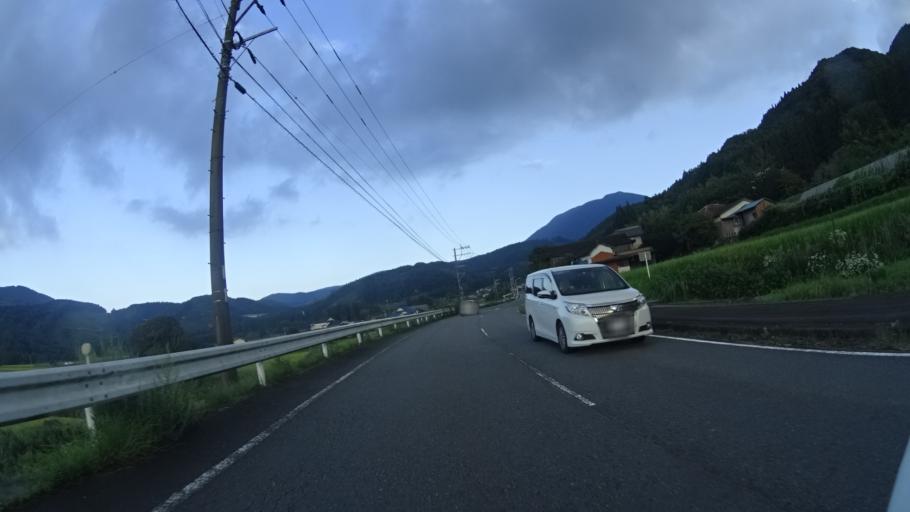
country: JP
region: Oita
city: Beppu
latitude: 33.3378
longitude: 131.4026
